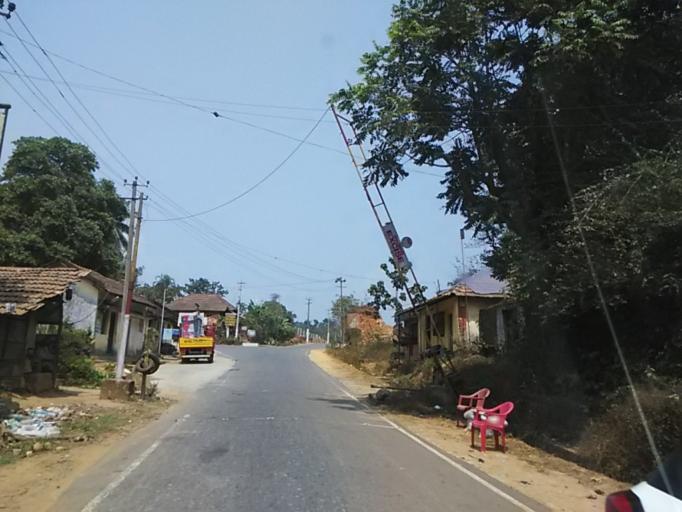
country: IN
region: Karnataka
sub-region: Kodagu
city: Virarajendrapet
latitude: 12.1444
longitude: 75.7950
